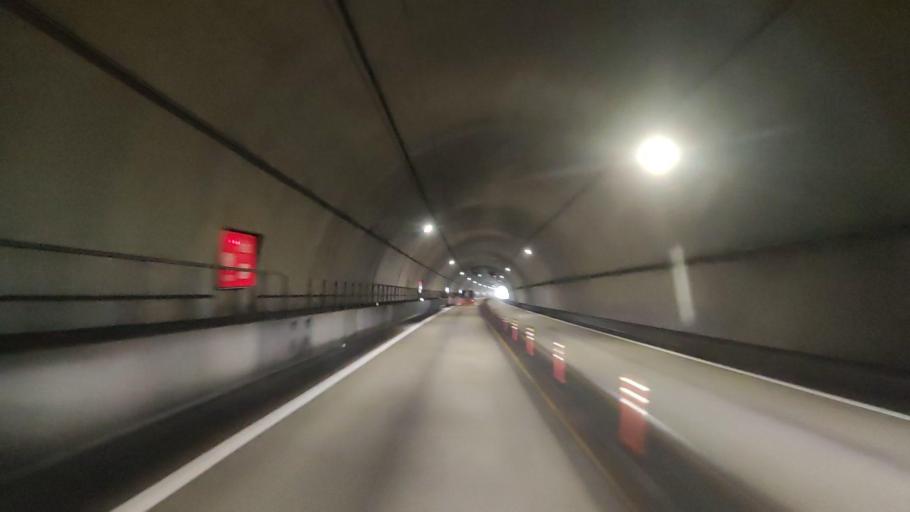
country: JP
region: Wakayama
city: Tanabe
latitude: 33.5503
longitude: 135.5152
